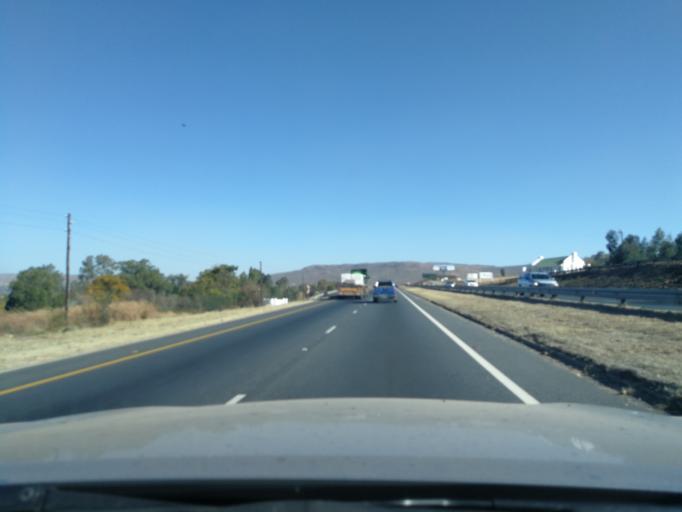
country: ZA
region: Gauteng
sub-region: West Rand District Municipality
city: Muldersdriseloop
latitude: -26.0487
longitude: 27.8400
